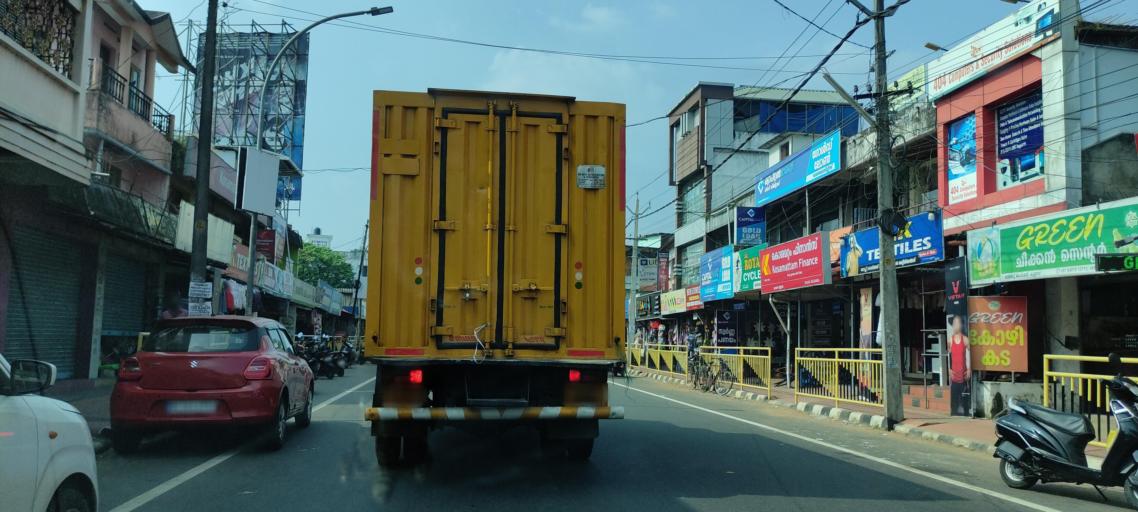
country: IN
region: Kerala
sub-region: Alappuzha
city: Chengannur
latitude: 9.2447
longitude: 76.6710
